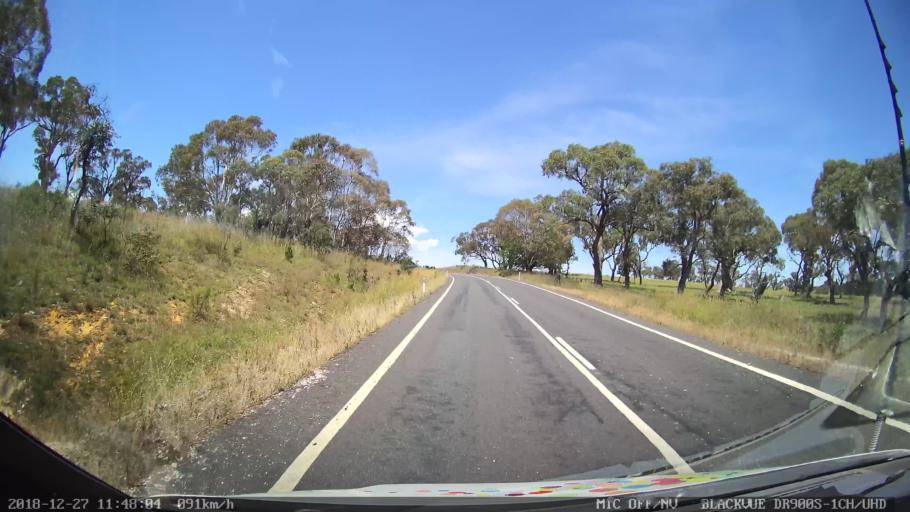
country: AU
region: New South Wales
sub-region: Bathurst Regional
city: Perthville
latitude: -33.6018
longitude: 149.4378
